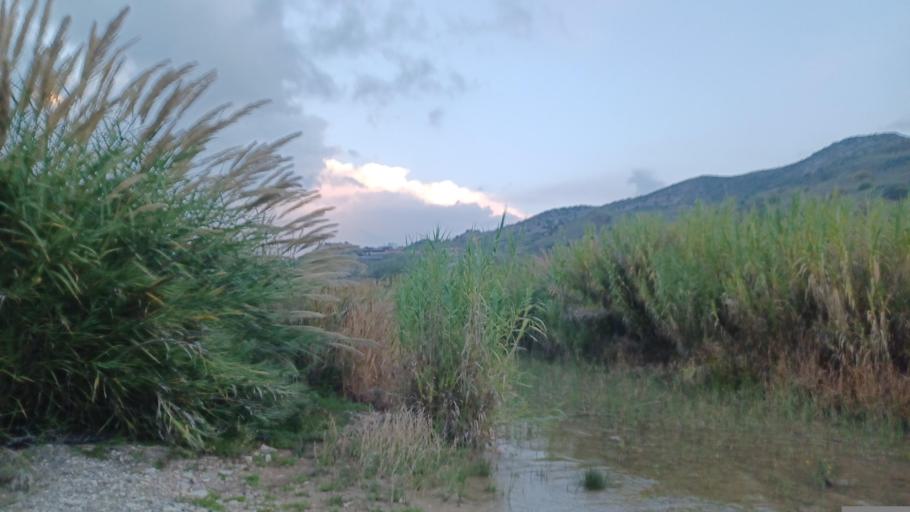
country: CY
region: Pafos
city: Mesogi
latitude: 34.7906
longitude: 32.5319
